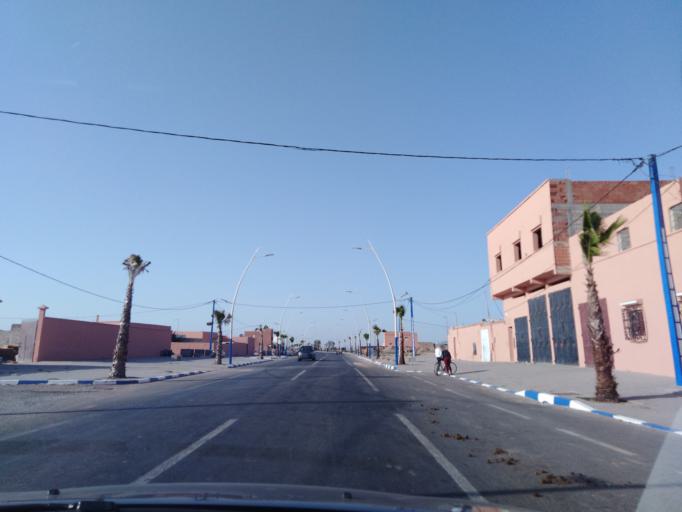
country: MA
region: Doukkala-Abda
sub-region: El-Jadida
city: Sidi Bennour
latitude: 32.5837
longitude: -8.7121
